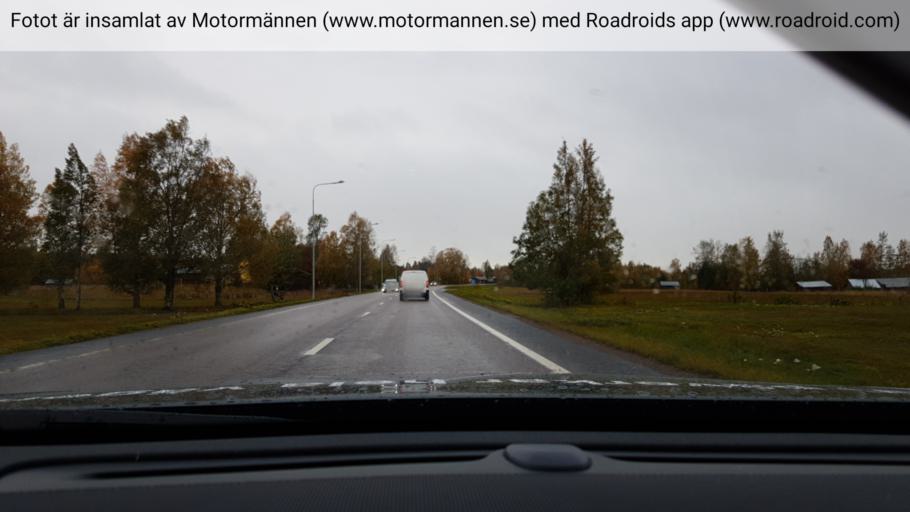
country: SE
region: Norrbotten
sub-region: Lulea Kommun
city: Gammelstad
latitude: 65.5832
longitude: 22.0369
